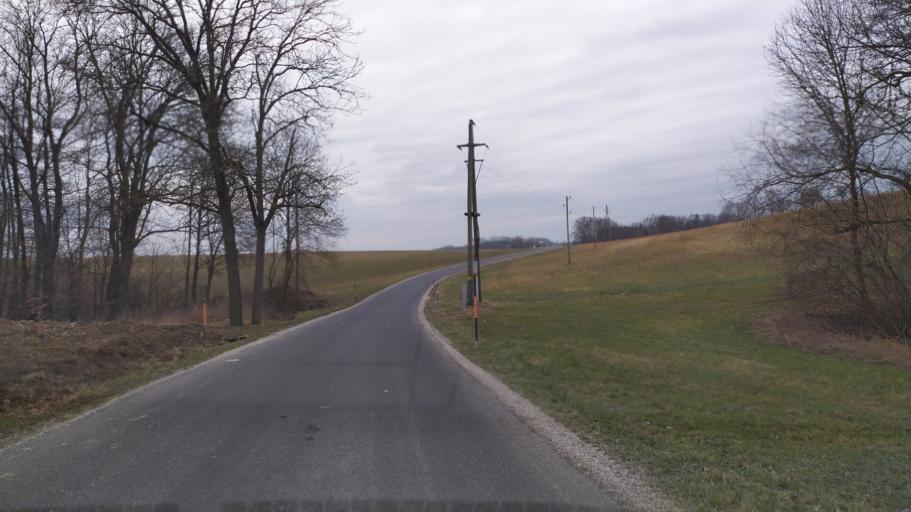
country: AT
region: Lower Austria
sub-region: Politischer Bezirk Amstetten
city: Strengberg
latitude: 48.1393
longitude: 14.7119
